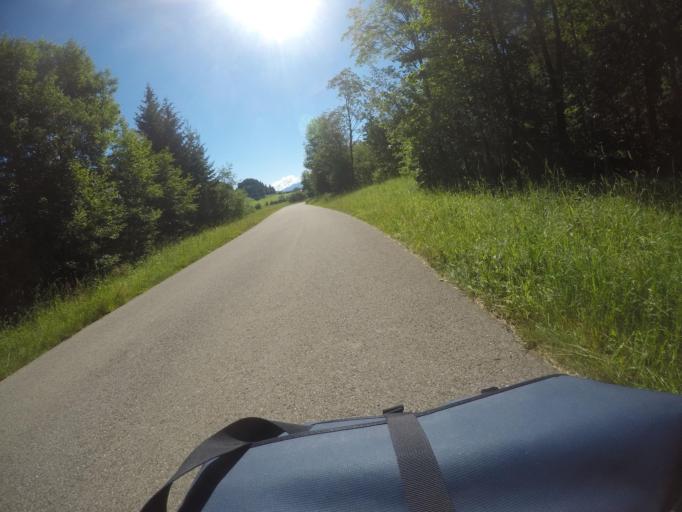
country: DE
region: Bavaria
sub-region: Swabia
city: Pfronten
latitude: 47.6078
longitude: 10.5403
